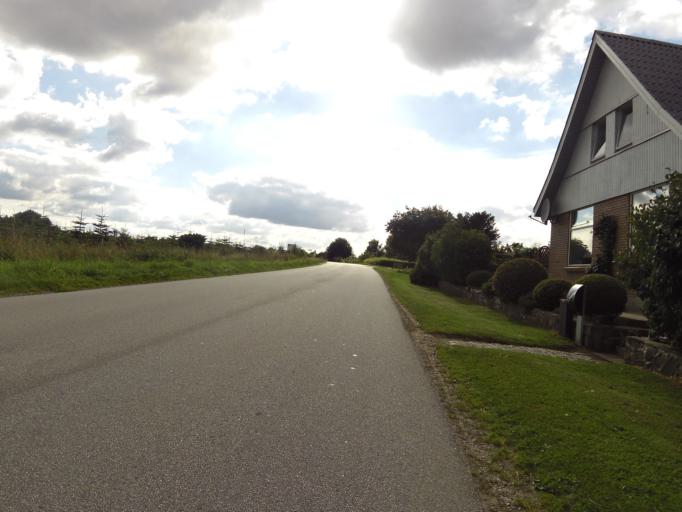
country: DK
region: South Denmark
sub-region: Haderslev Kommune
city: Haderslev
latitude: 55.2076
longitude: 9.4356
